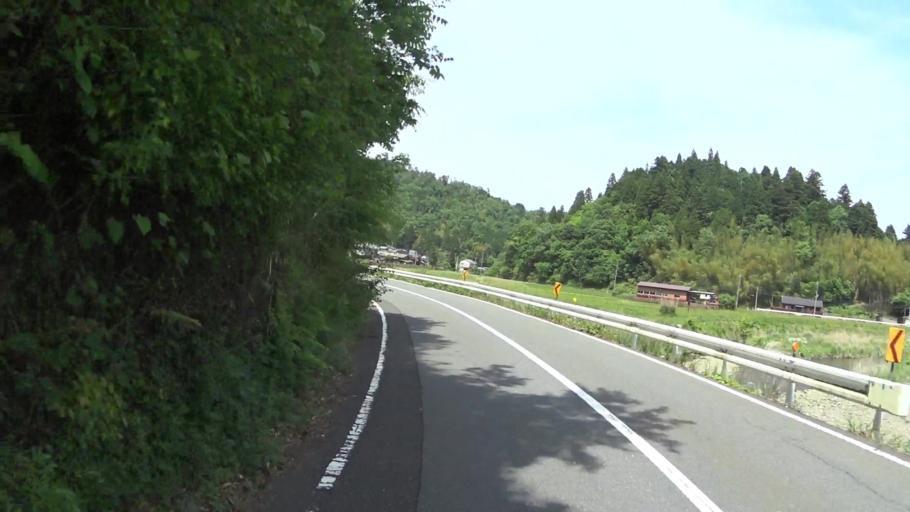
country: JP
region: Kyoto
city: Maizuru
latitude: 35.3851
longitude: 135.4607
